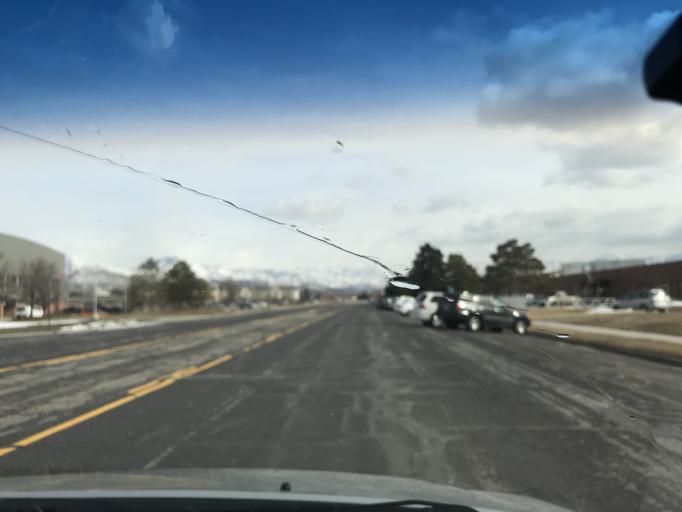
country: US
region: Utah
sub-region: Salt Lake County
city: Salt Lake City
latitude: 40.7714
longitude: -111.9571
